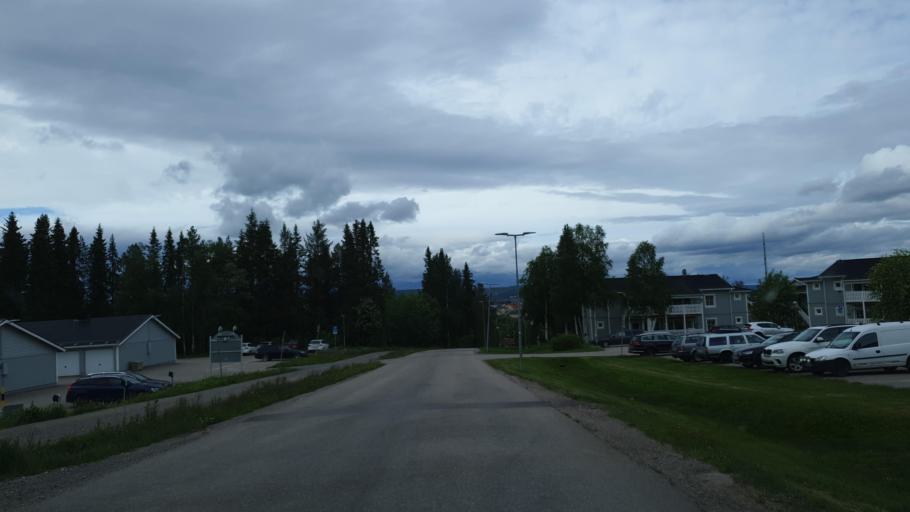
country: SE
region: Norrbotten
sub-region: Gallivare Kommun
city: Gaellivare
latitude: 67.1252
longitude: 20.6563
